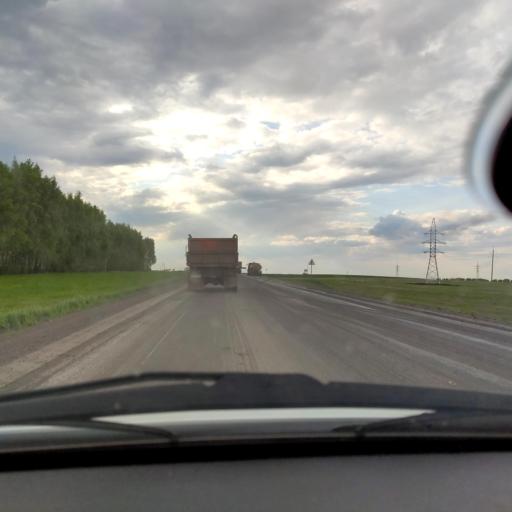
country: RU
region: Bashkortostan
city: Dyurtyuli
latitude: 55.3349
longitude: 54.9539
